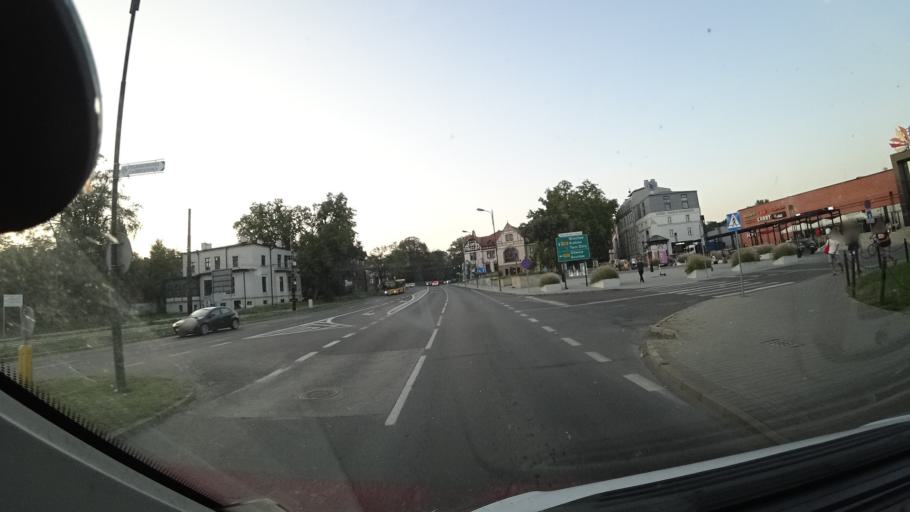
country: PL
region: Silesian Voivodeship
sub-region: Zabrze
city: Zabrze
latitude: 50.3105
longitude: 18.7855
